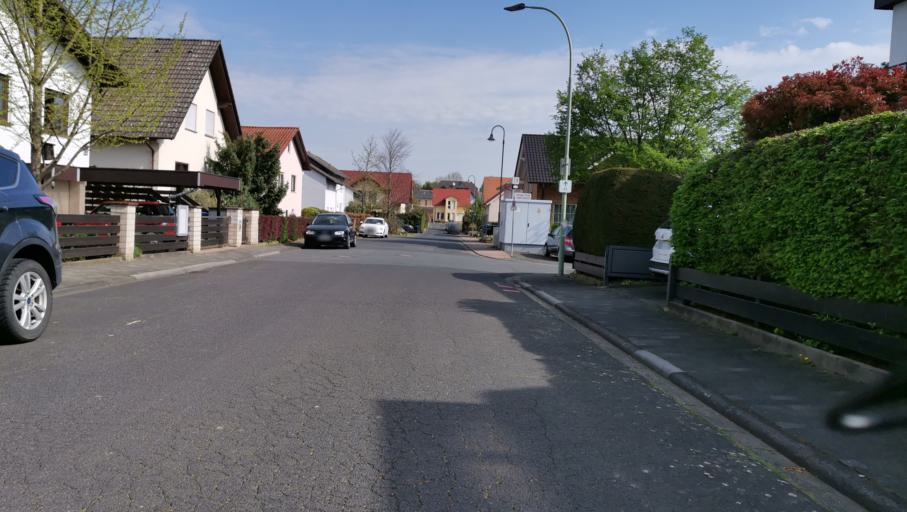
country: DE
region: Hesse
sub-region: Regierungsbezirk Darmstadt
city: Karben
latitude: 50.2448
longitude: 8.7119
